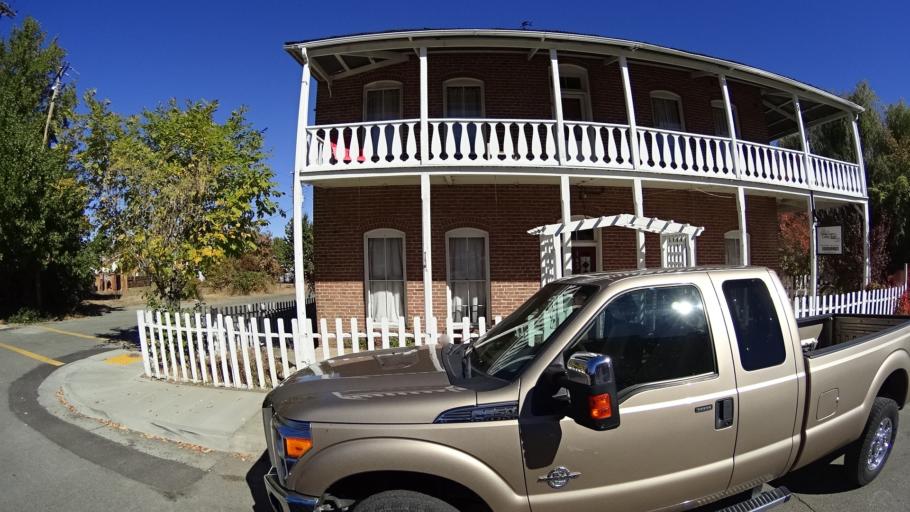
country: US
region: California
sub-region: Siskiyou County
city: Yreka
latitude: 41.4578
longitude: -122.8940
